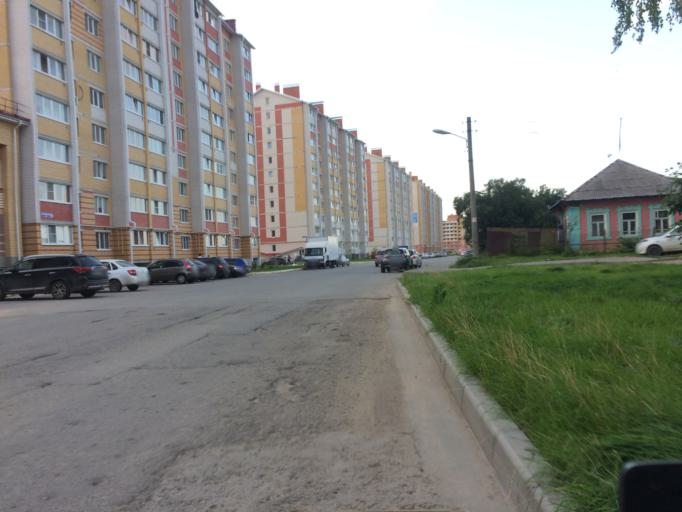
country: RU
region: Mariy-El
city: Medvedevo
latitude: 56.6460
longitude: 47.8350
